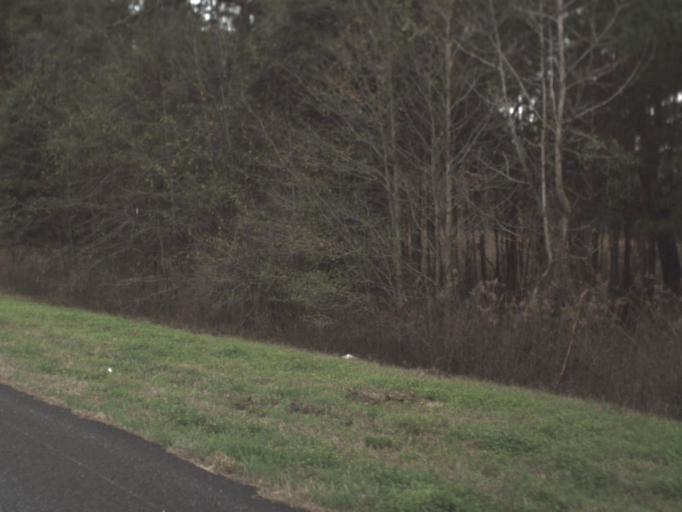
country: US
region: Florida
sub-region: Leon County
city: Tallahassee
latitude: 30.6076
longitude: -84.1786
